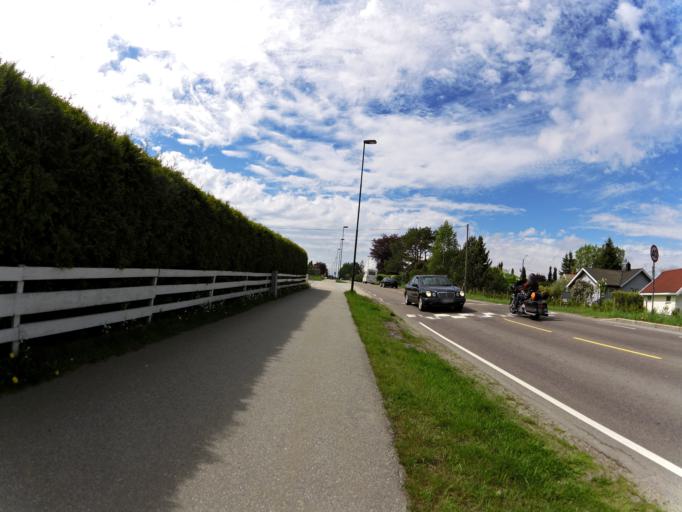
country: NO
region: Ostfold
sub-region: Rade
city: Karlshus
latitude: 59.3534
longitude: 10.8646
